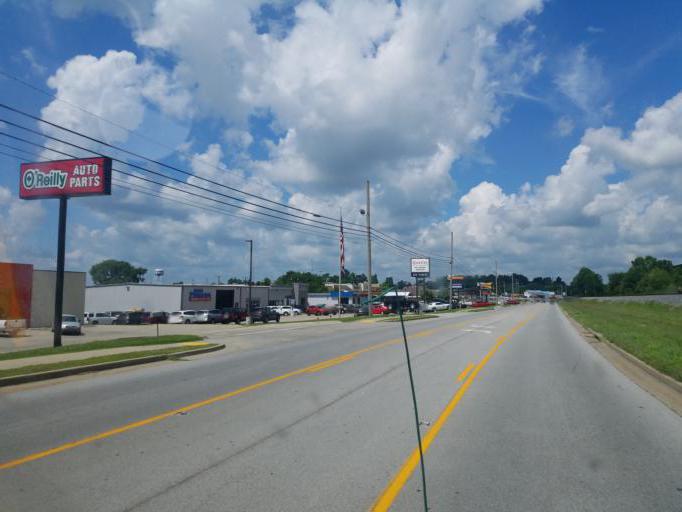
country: US
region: Kentucky
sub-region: Grayson County
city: Leitchfield
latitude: 37.4854
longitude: -86.2708
